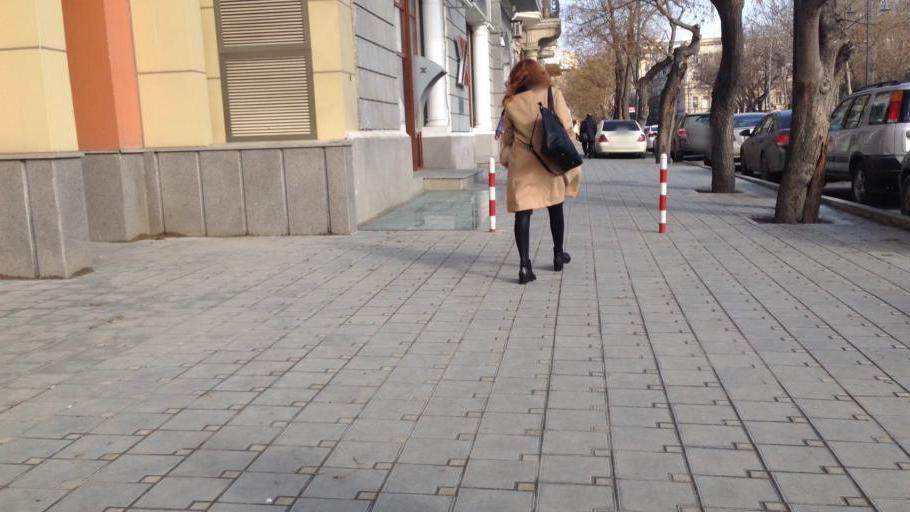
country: AZ
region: Baki
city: Baku
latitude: 40.3733
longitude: 49.8450
